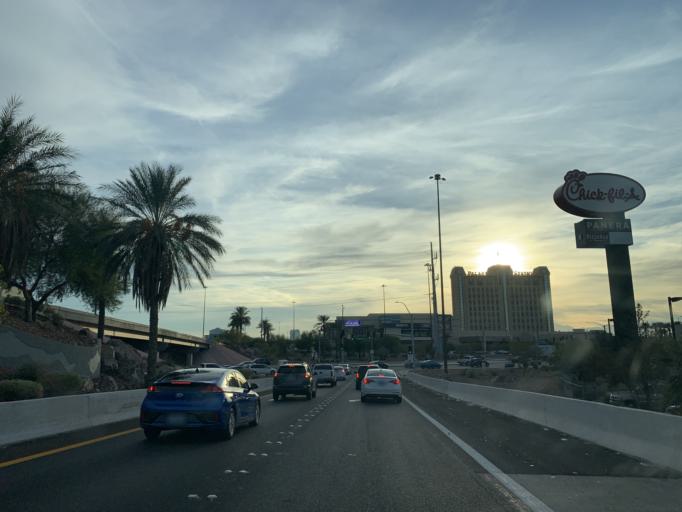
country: US
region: Nevada
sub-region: Clark County
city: Las Vegas
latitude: 36.1449
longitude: -115.1712
